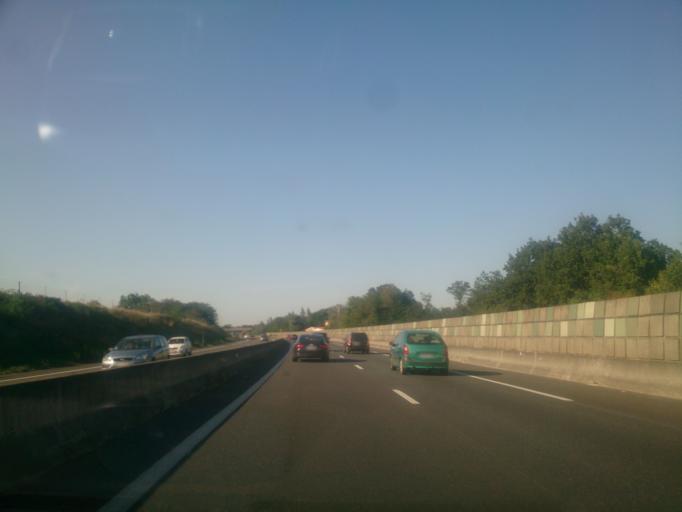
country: FR
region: Midi-Pyrenees
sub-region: Departement du Tarn-et-Garonne
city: Montauban
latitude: 44.0125
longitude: 1.3865
